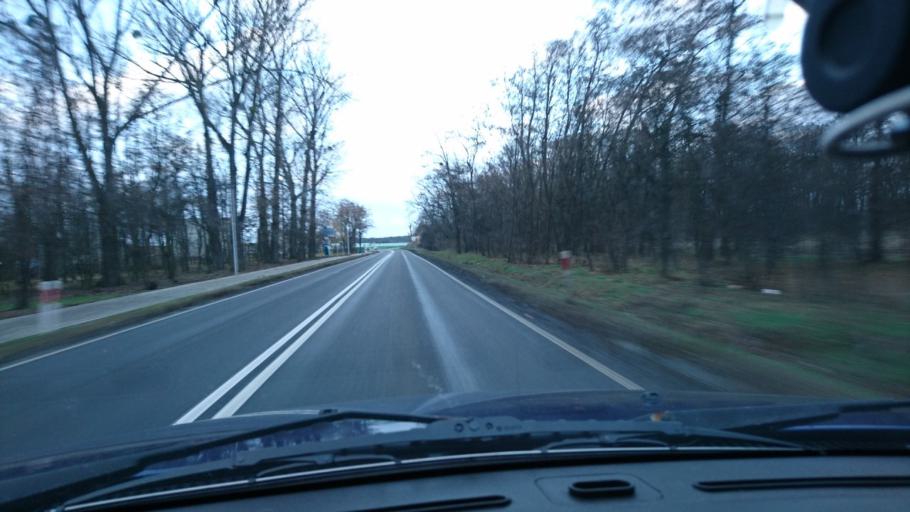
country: PL
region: Greater Poland Voivodeship
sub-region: Powiat kepinski
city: Kepno
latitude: 51.3130
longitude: 17.9840
